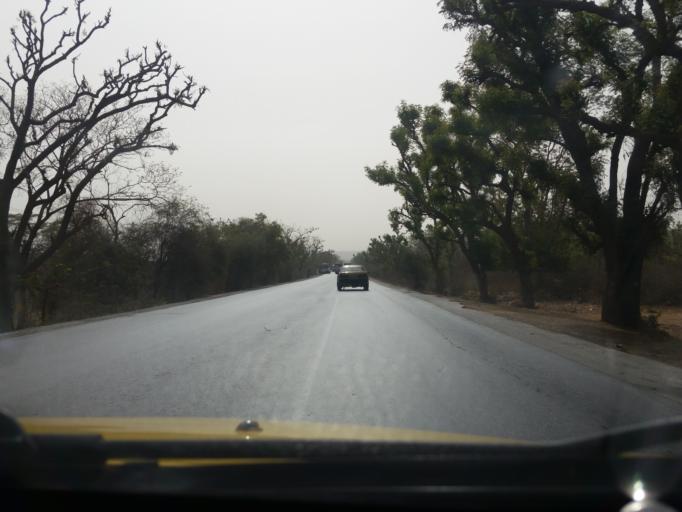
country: SN
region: Thies
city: Pout
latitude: 14.7619
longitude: -17.0334
